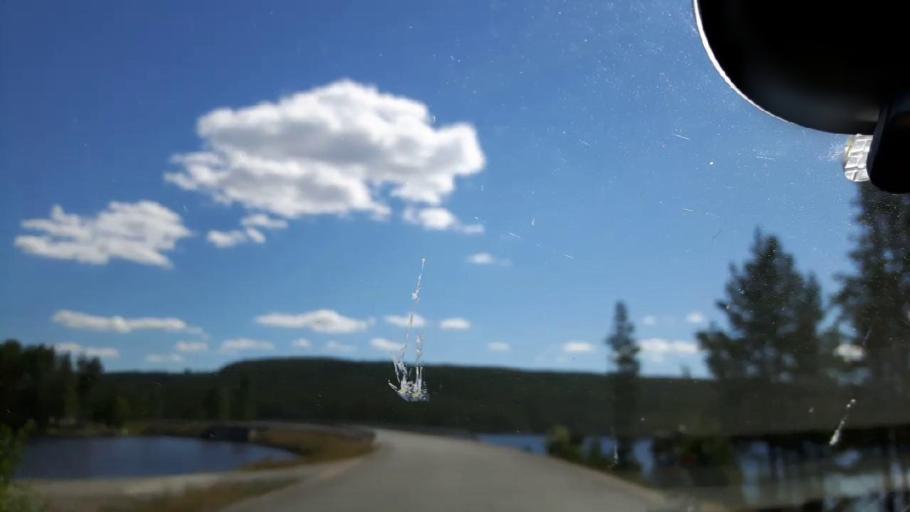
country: SE
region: Vaesternorrland
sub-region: Ange Kommun
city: Fransta
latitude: 62.6949
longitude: 16.3900
